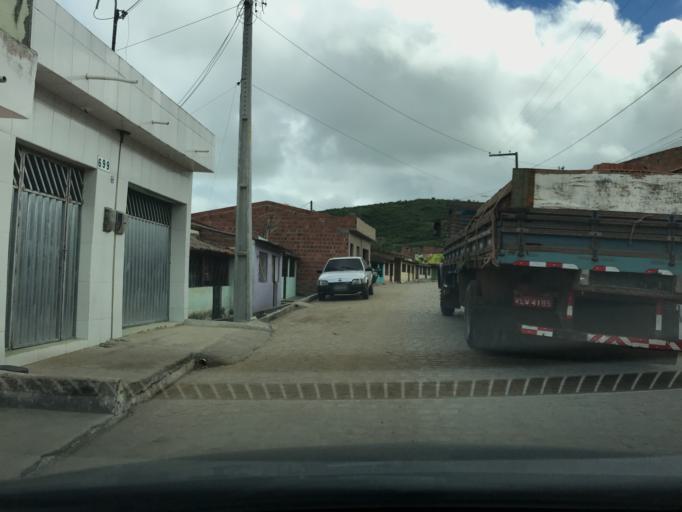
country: BR
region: Pernambuco
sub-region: Bezerros
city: Bezerros
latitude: -8.2289
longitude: -35.7606
